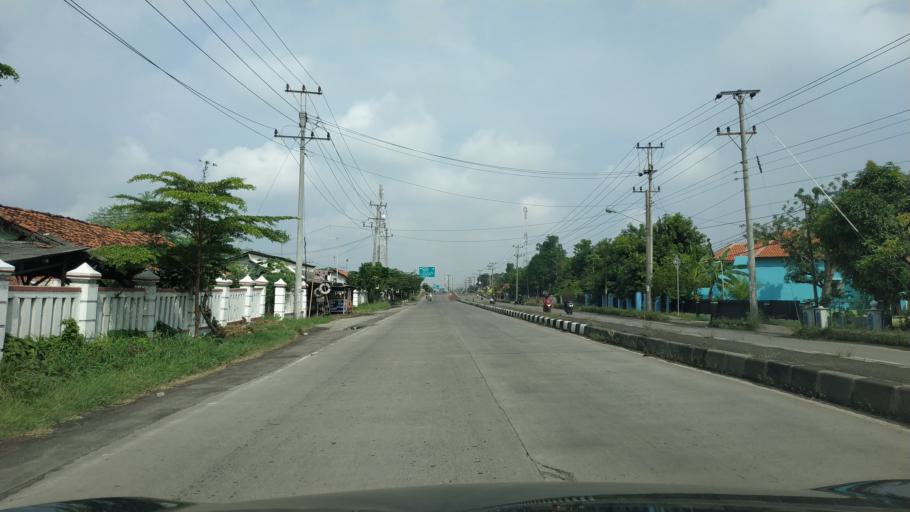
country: ID
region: Central Java
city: Bulakamba
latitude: -6.8718
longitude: 108.8900
